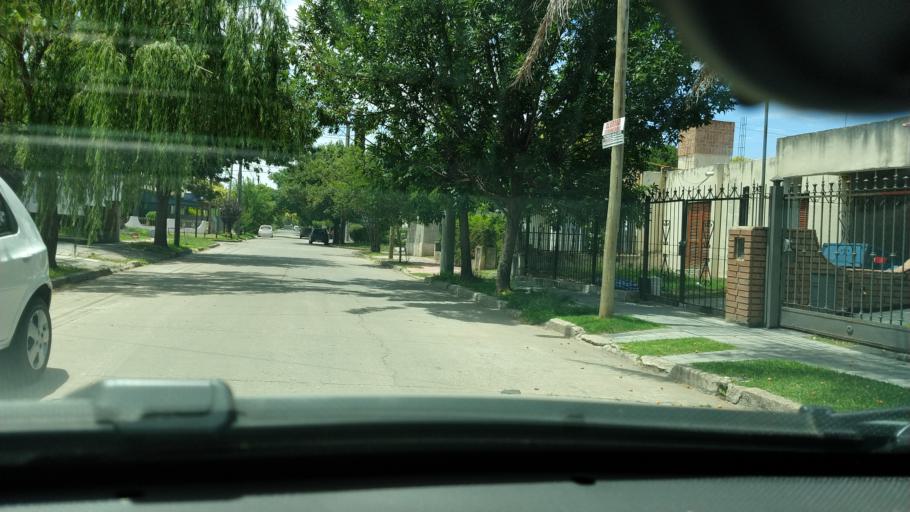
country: AR
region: Cordoba
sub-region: Departamento de Capital
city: Cordoba
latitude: -31.3600
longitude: -64.2303
